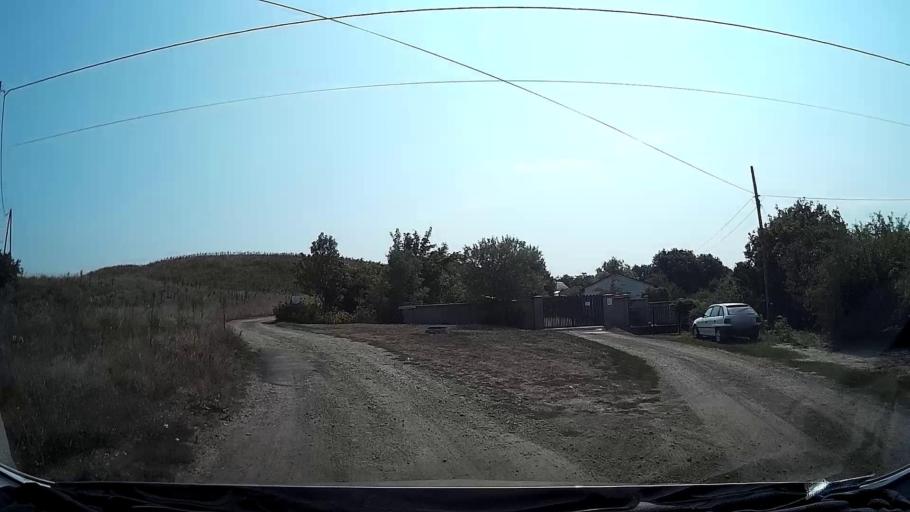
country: HU
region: Pest
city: Szentendre
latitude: 47.6892
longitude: 19.0392
